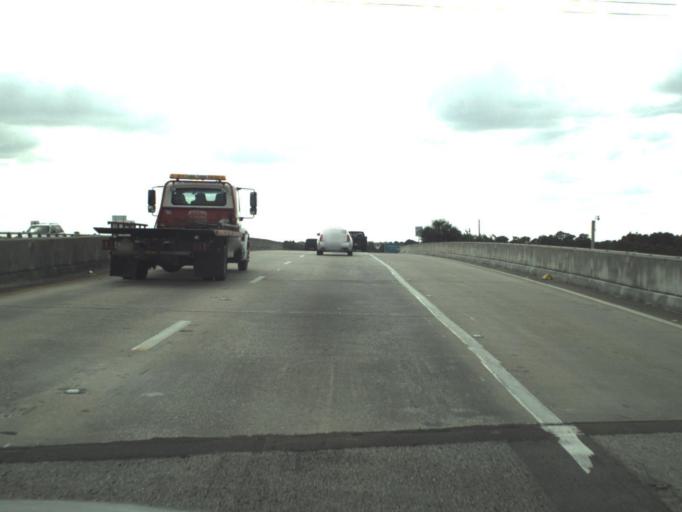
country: US
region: Florida
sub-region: Brevard County
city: Cocoa
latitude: 28.4005
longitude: -80.7524
